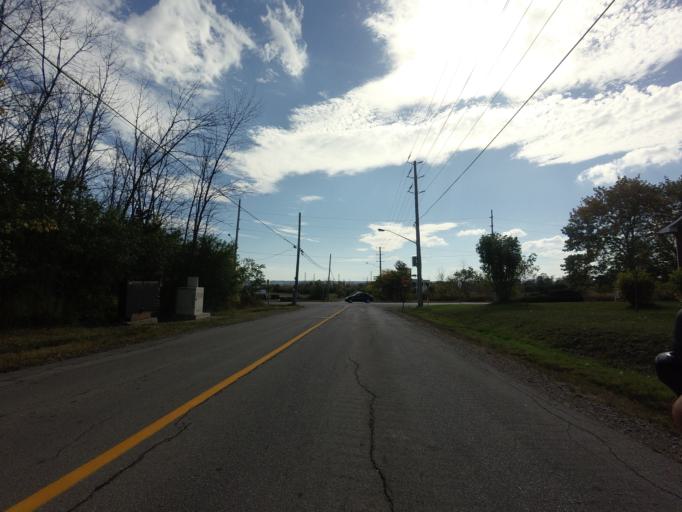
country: CA
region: Ontario
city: Hamilton
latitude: 43.2979
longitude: -79.9078
